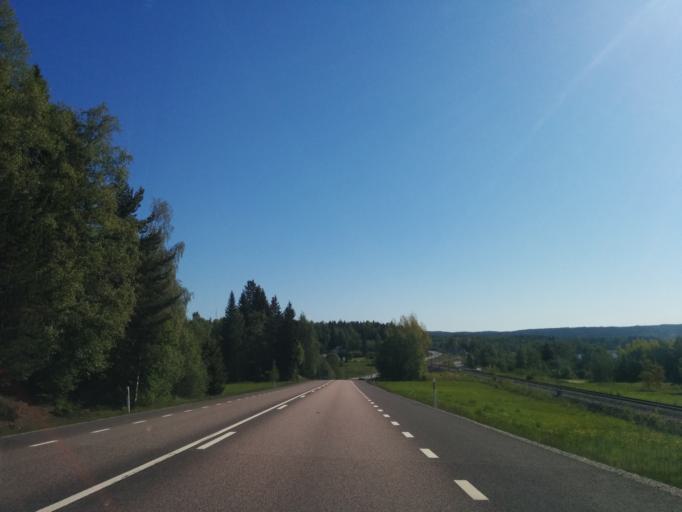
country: SE
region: Vaesternorrland
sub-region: Kramfors Kommun
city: Kramfors
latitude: 62.8284
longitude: 17.8529
